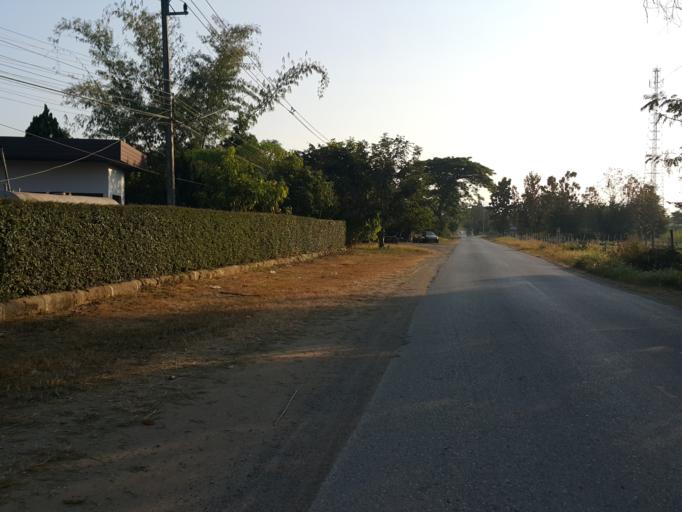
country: TH
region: Chiang Mai
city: Mae On
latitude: 18.7823
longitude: 99.2566
